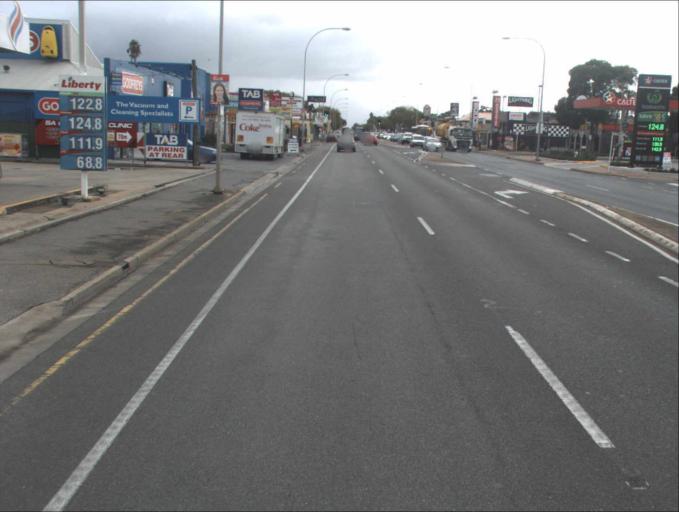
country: AU
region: South Australia
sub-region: Prospect
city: Prospect
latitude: -34.8884
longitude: 138.6030
